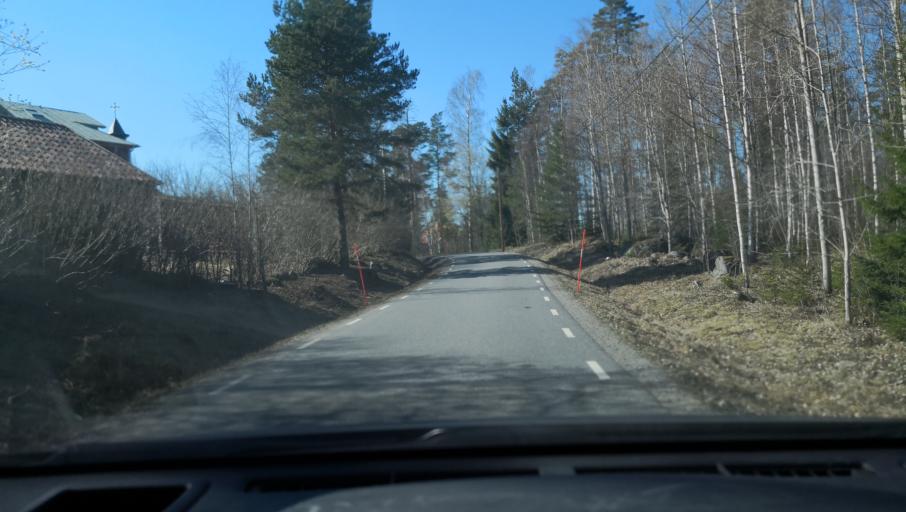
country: SE
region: Vaestmanland
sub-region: Sala Kommun
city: Sala
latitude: 59.9271
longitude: 16.4686
